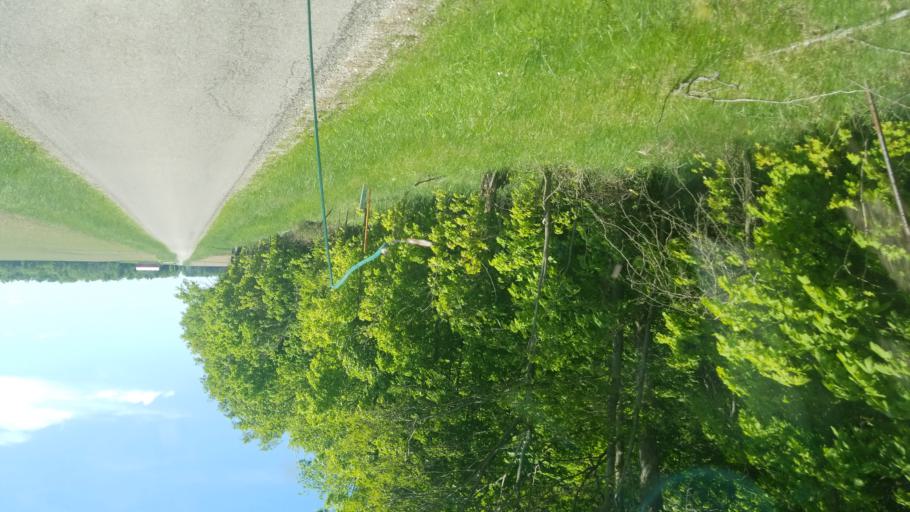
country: US
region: Ohio
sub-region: Crawford County
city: Bucyrus
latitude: 40.9427
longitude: -83.0356
